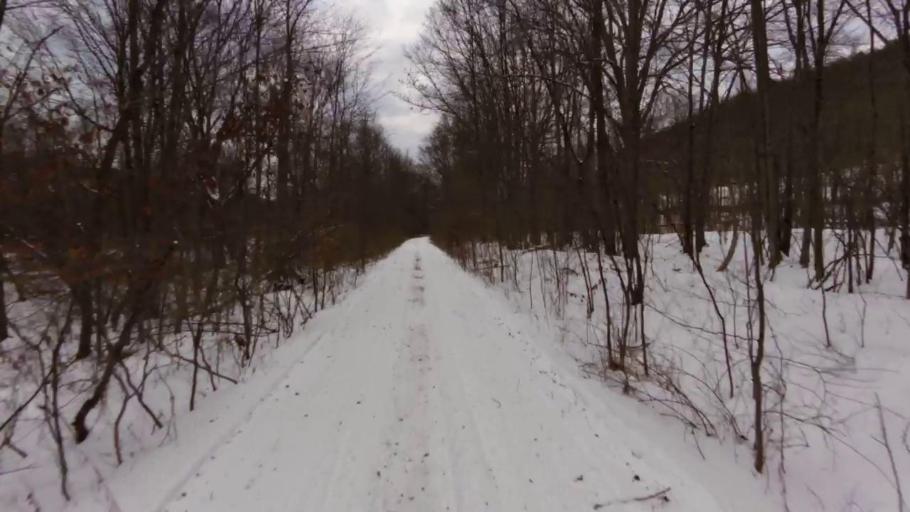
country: US
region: Pennsylvania
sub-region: McKean County
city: Foster Brook
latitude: 42.0568
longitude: -78.6373
